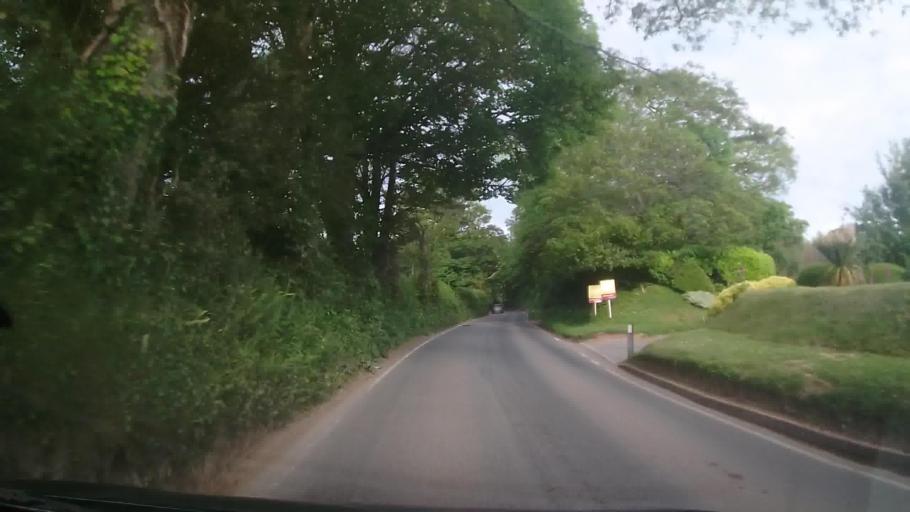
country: GB
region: England
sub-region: Devon
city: Kingsbridge
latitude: 50.2988
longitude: -3.8086
